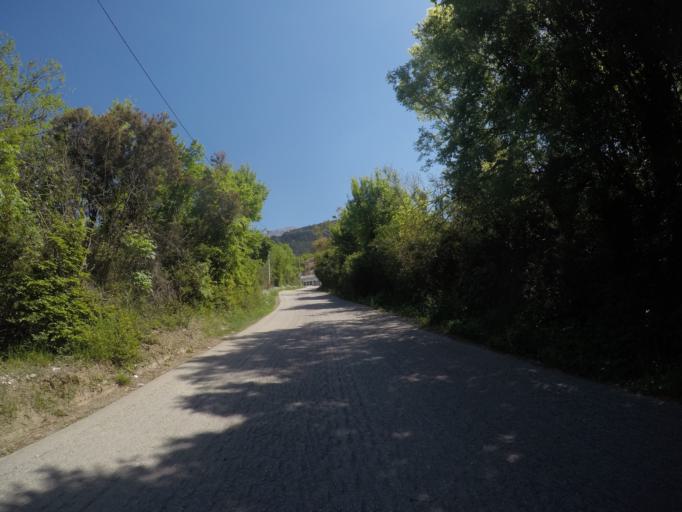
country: ME
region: Kotor
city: Kotor
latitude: 42.3998
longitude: 18.7513
